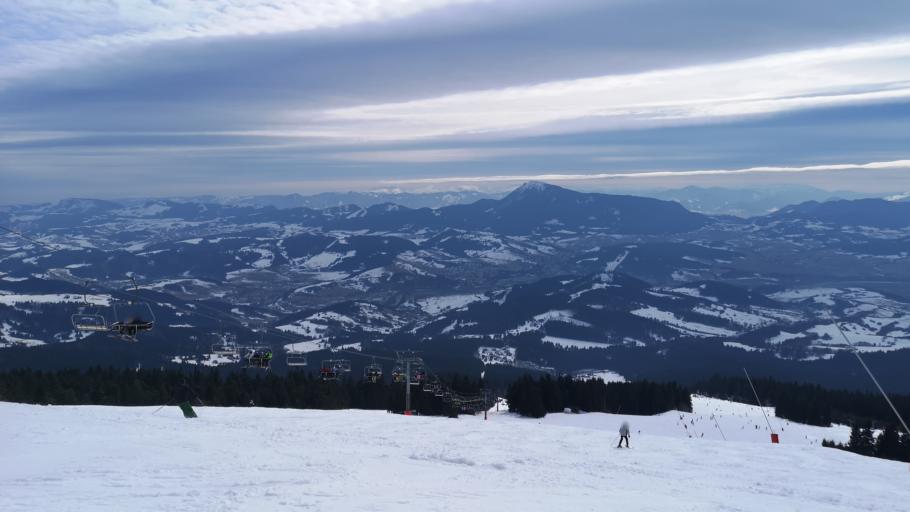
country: SK
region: Zilinsky
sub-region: Okres Dolny Kubin
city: Dolny Kubin
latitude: 49.2698
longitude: 19.2548
